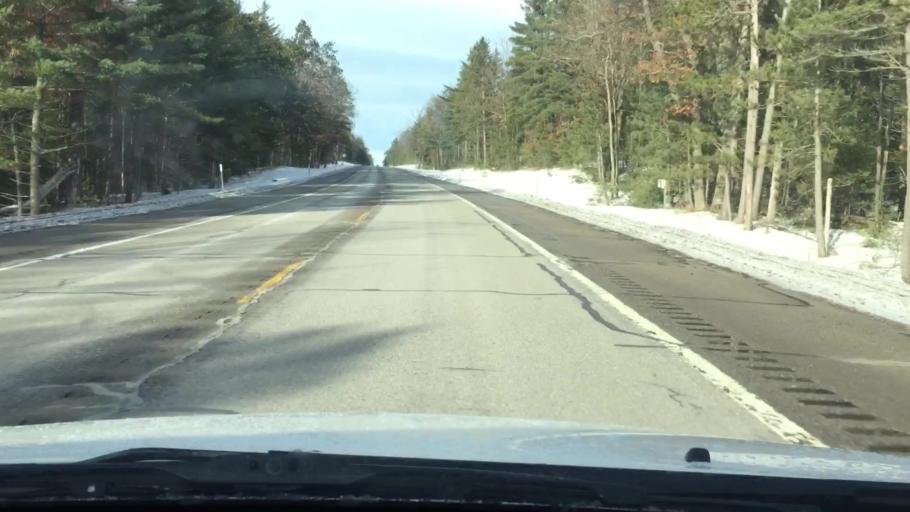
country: US
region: Michigan
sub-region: Wexford County
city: Manton
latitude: 44.5476
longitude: -85.3702
